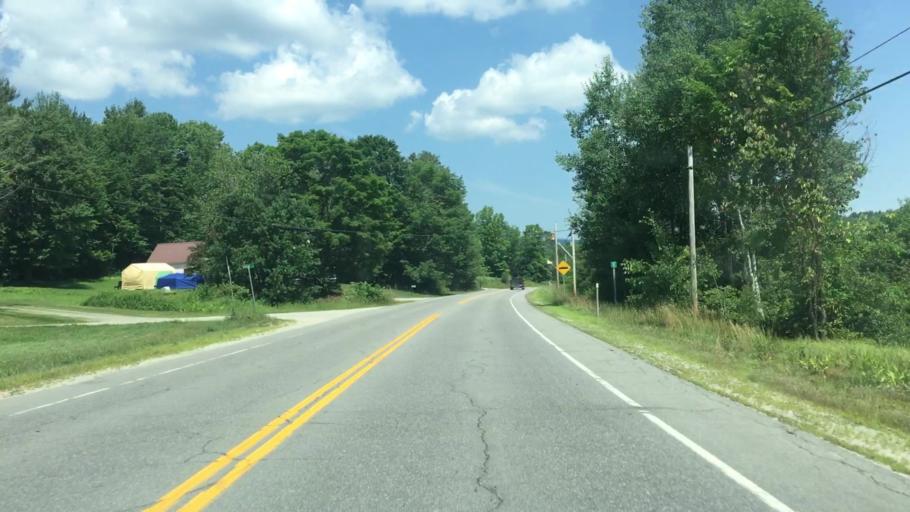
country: US
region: New Hampshire
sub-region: Sullivan County
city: Grantham
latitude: 43.4480
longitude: -72.1612
